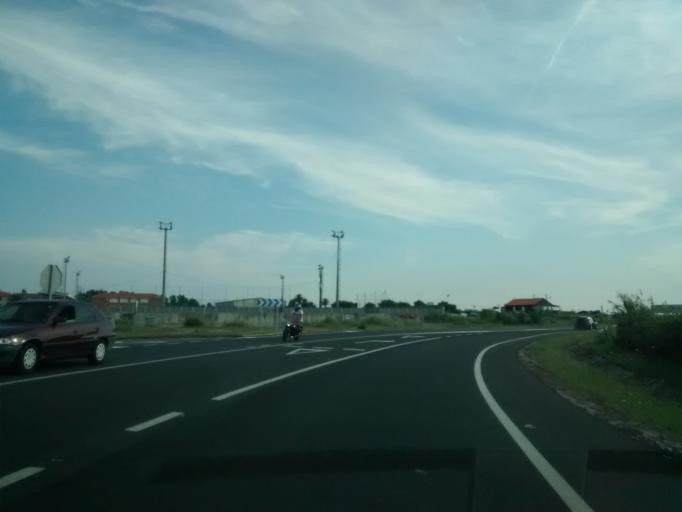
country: ES
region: Galicia
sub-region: Provincia de Pontevedra
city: O Grove
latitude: 42.4405
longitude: -8.8692
